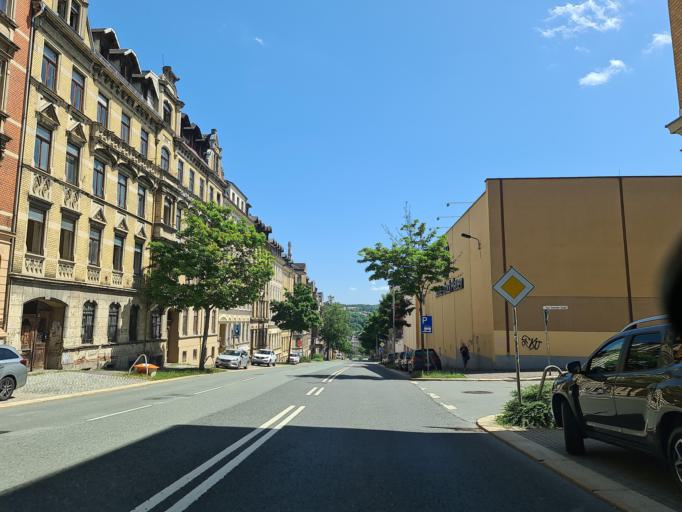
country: DE
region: Saxony
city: Plauen
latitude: 50.5045
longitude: 12.1423
